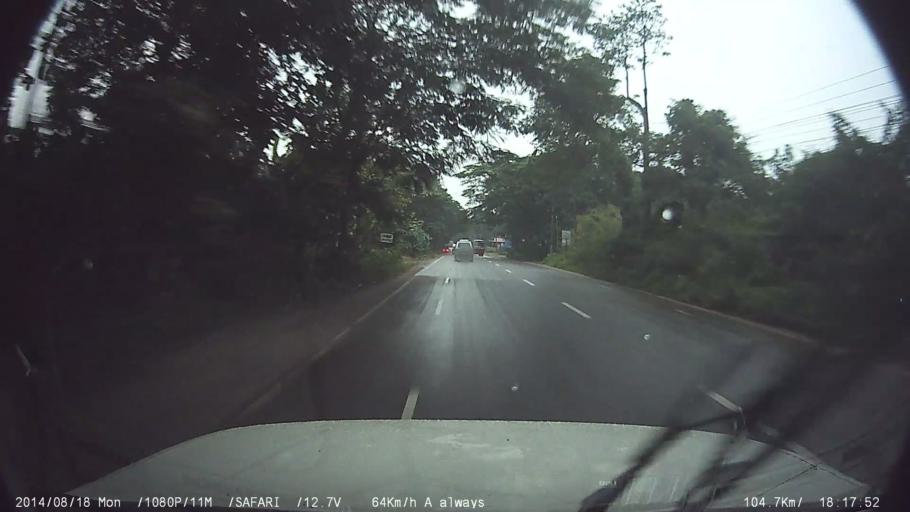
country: IN
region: Kerala
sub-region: Ernakulam
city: Muvattupula
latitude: 10.0419
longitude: 76.5373
